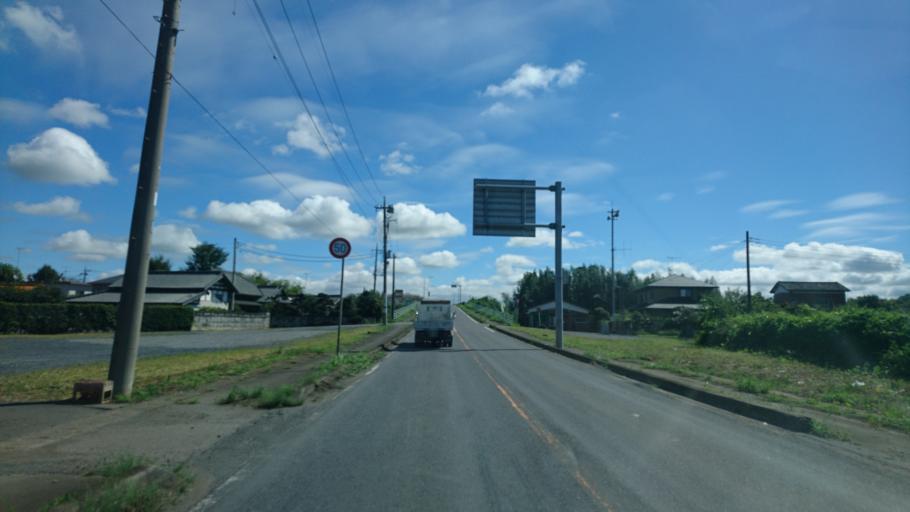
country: JP
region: Ibaraki
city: Yuki
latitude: 36.2173
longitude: 139.9134
